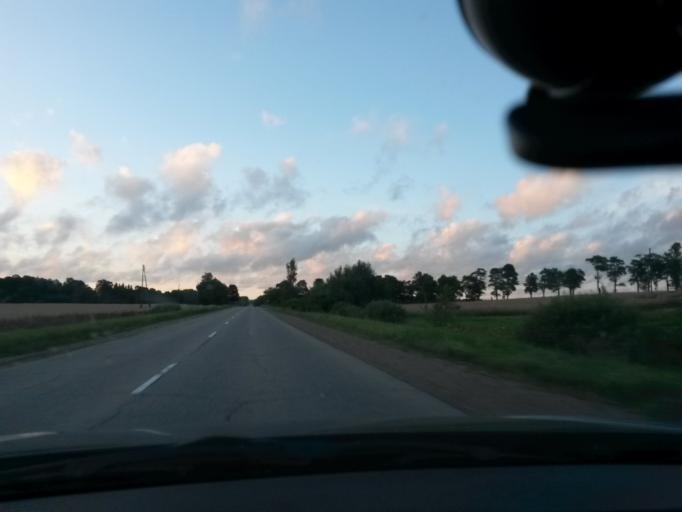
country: LV
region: Madonas Rajons
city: Madona
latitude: 56.7444
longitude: 26.0218
